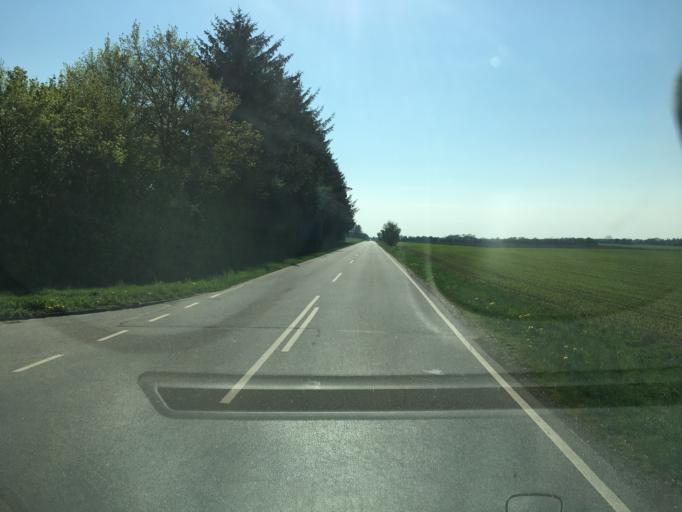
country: DK
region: South Denmark
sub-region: Haderslev Kommune
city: Vojens
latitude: 55.3093
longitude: 9.2782
